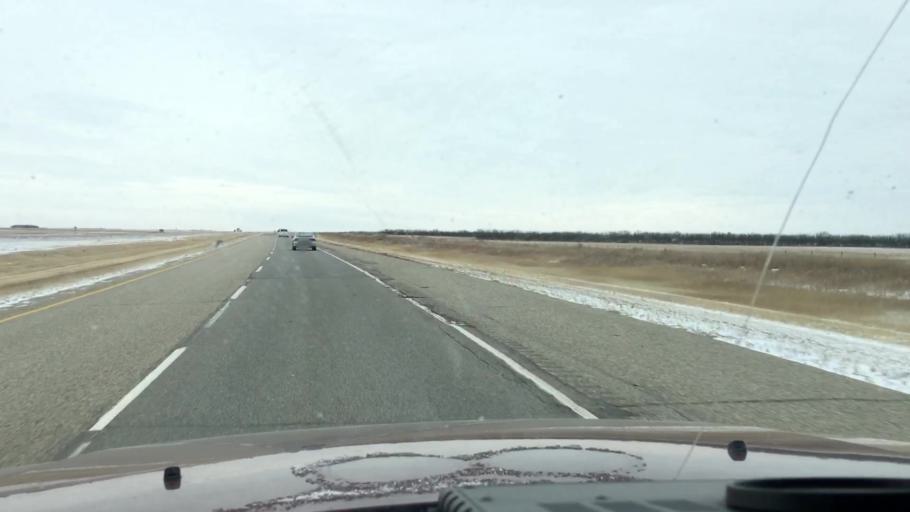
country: CA
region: Saskatchewan
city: Saskatoon
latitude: 51.4700
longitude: -106.2463
